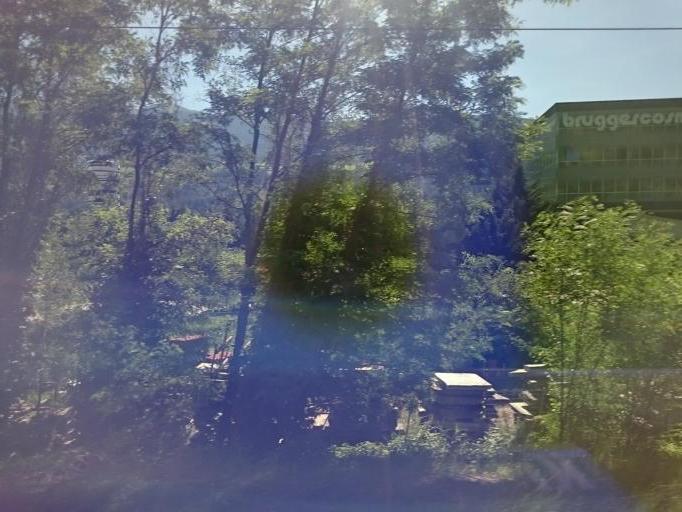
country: IT
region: Trentino-Alto Adige
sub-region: Bolzano
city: Bressanone
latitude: 46.6965
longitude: 11.6439
